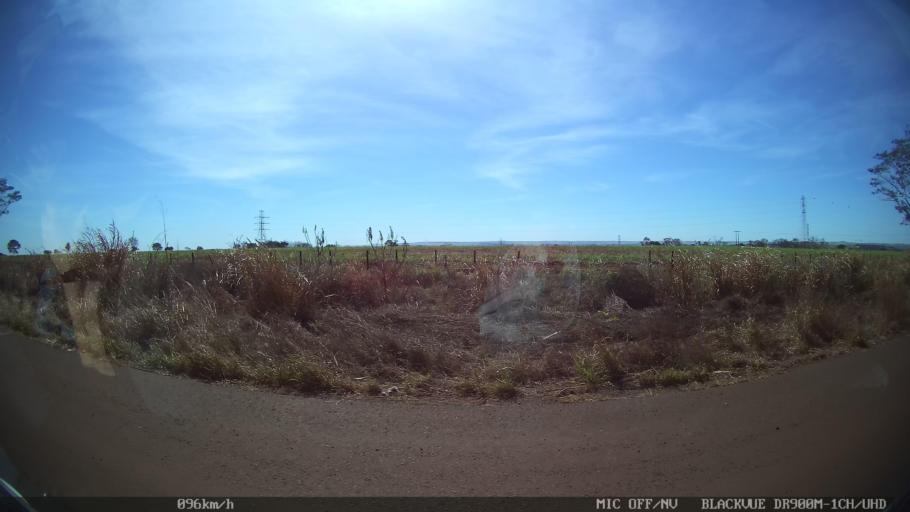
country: BR
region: Sao Paulo
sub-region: Sao Joaquim Da Barra
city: Sao Joaquim da Barra
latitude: -20.5225
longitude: -47.8535
